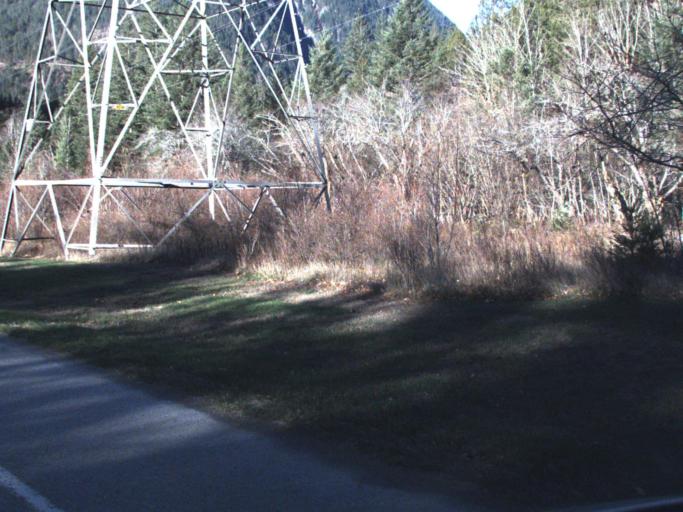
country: US
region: Washington
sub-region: Snohomish County
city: Darrington
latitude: 48.6729
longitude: -121.2577
